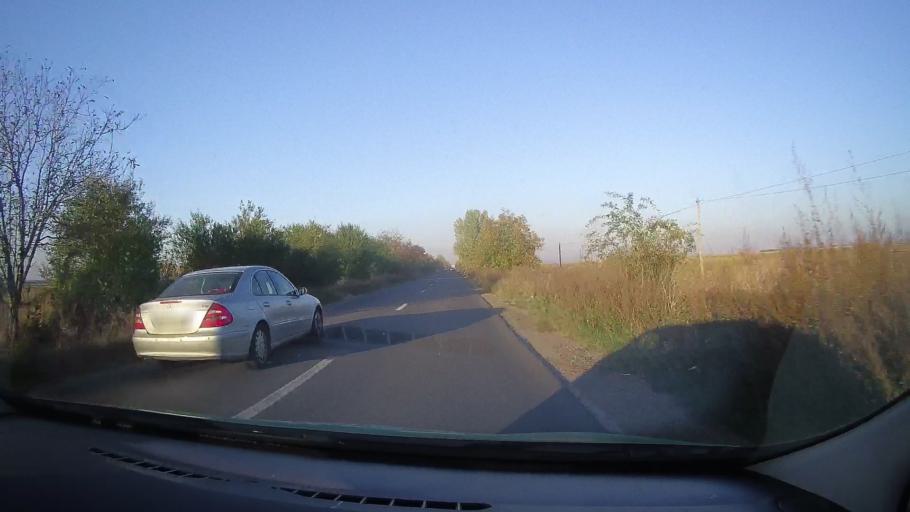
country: RO
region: Bihor
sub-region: Comuna Salard
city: Salard
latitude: 47.1926
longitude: 21.9972
